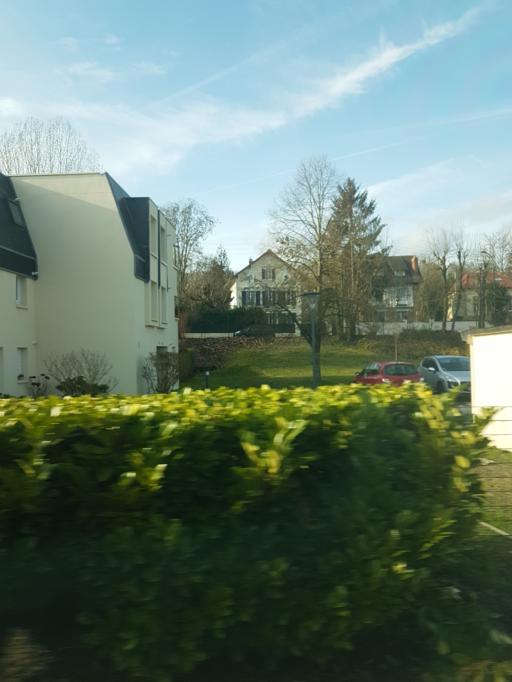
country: FR
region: Ile-de-France
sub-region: Departement des Yvelines
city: Bougival
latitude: 48.8529
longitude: 2.1316
